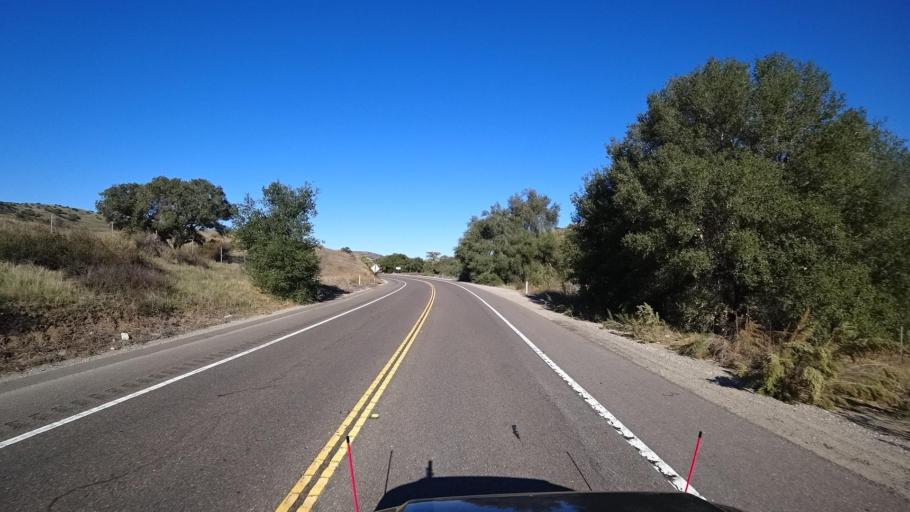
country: US
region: California
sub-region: San Diego County
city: Jamul
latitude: 32.6635
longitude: -116.8139
